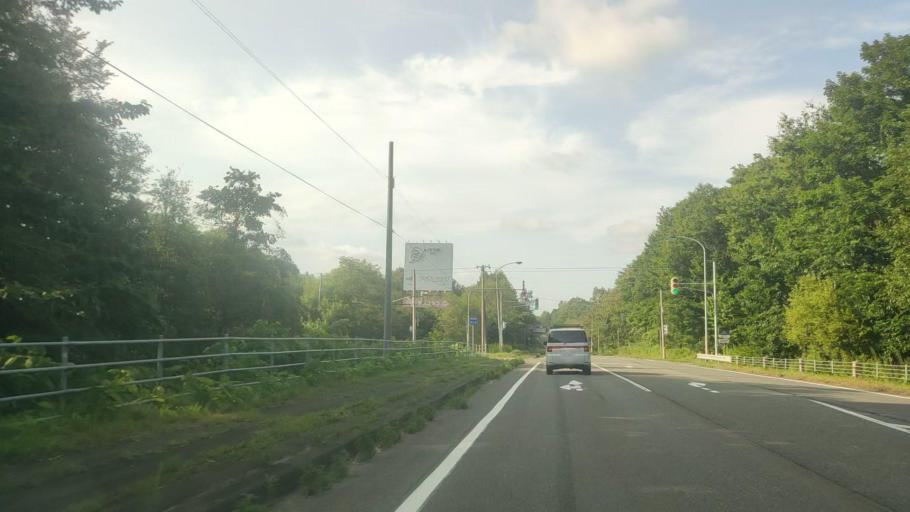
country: JP
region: Hokkaido
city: Chitose
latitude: 42.8660
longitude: 141.8226
